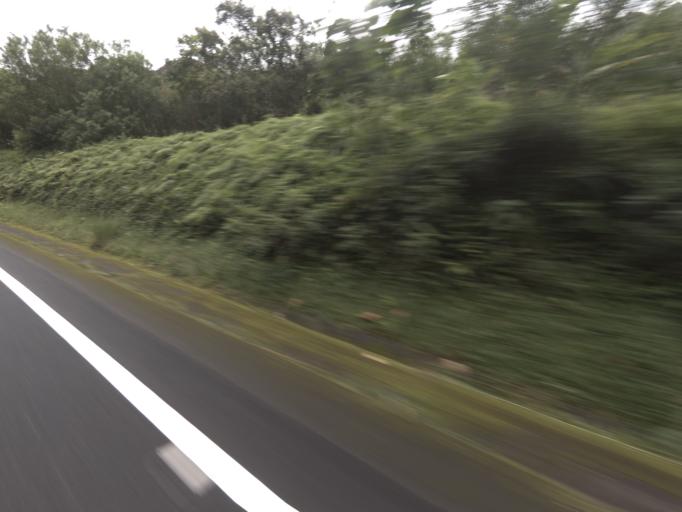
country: US
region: Hawaii
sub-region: Honolulu County
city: Kane'ohe
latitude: 21.3893
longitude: -157.8169
